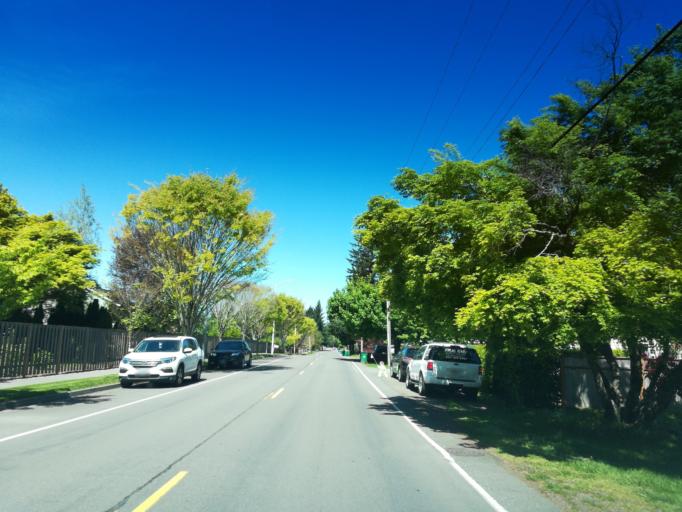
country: US
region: Oregon
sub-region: Multnomah County
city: Troutdale
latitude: 45.5286
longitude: -122.3933
